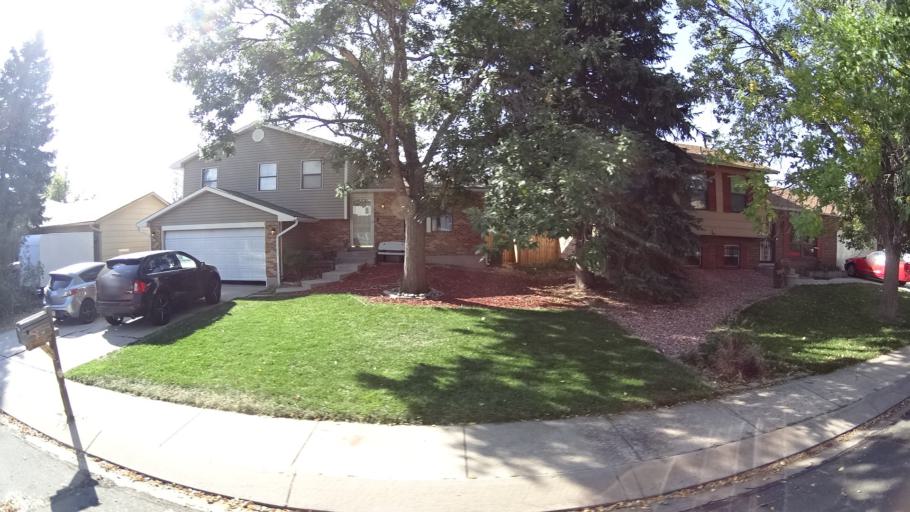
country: US
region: Colorado
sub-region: El Paso County
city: Cimarron Hills
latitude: 38.8826
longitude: -104.7233
